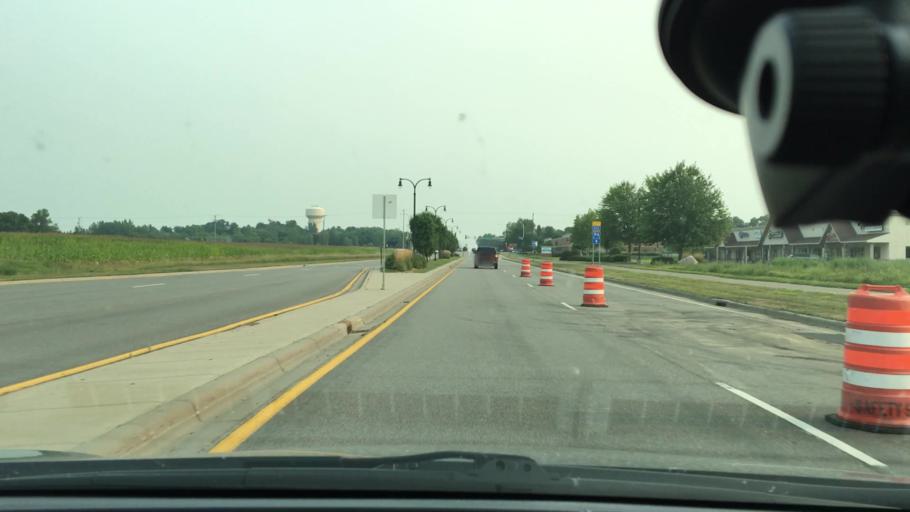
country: US
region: Minnesota
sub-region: Wright County
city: Albertville
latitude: 45.2279
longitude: -93.6645
